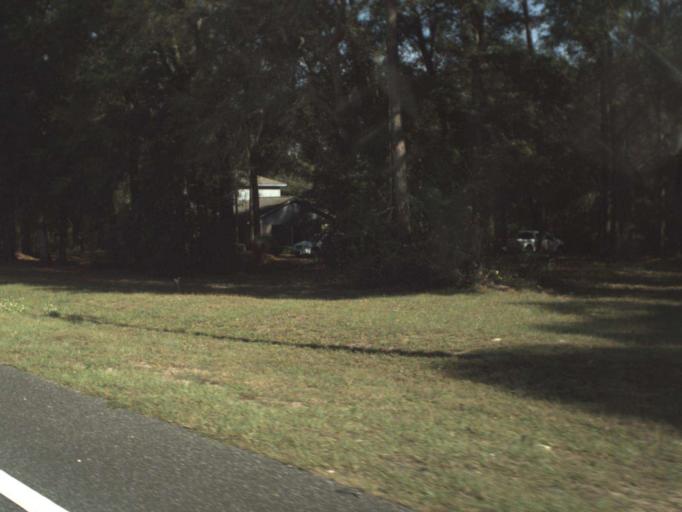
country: US
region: Florida
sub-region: Gadsden County
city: Havana
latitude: 30.5668
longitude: -84.3919
